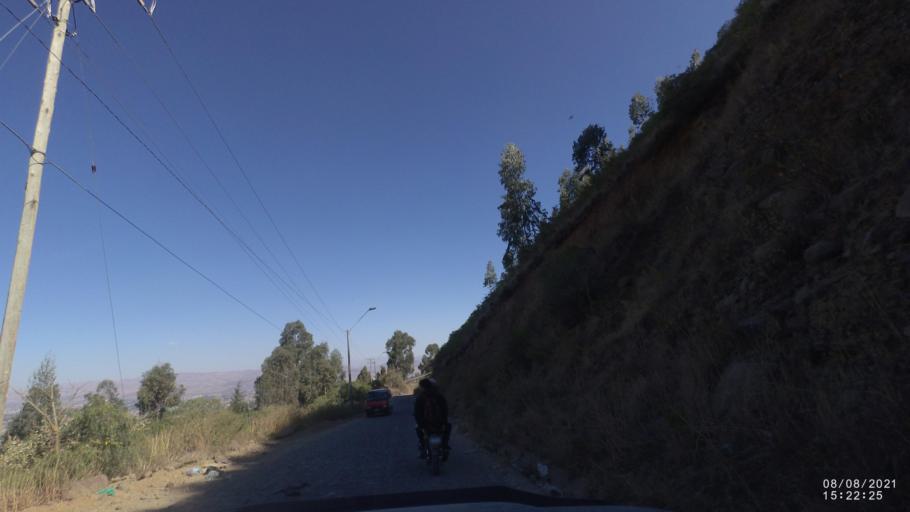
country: BO
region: Cochabamba
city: Cochabamba
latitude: -17.3084
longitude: -66.2941
